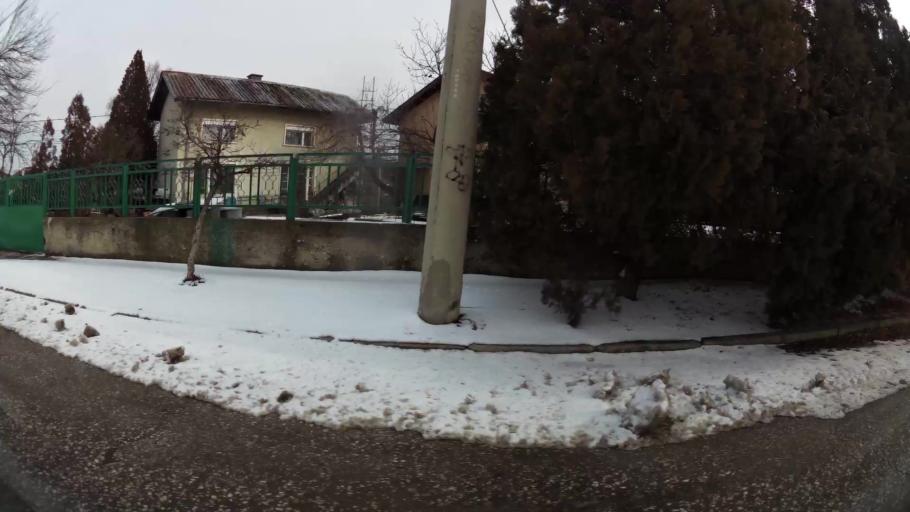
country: BG
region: Sofia-Capital
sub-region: Stolichna Obshtina
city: Sofia
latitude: 42.7155
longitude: 23.4038
